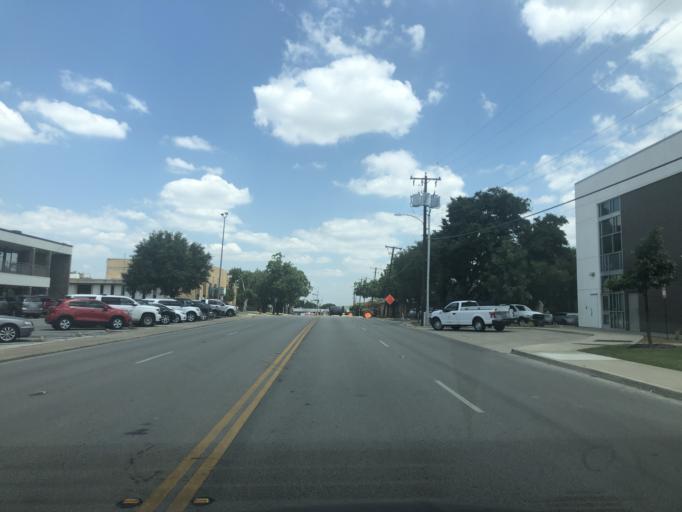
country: US
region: Texas
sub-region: Dallas County
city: Grand Prairie
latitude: 32.7470
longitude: -97.0052
